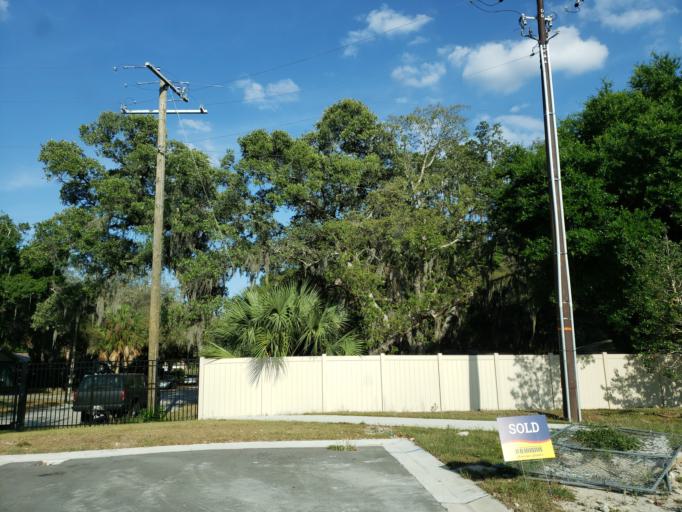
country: US
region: Florida
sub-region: Hillsborough County
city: Brandon
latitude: 27.9082
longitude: -82.2818
